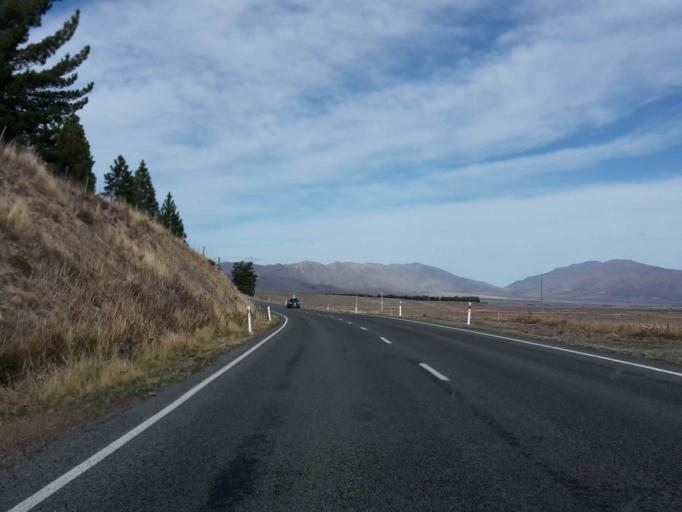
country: NZ
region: Canterbury
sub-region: Timaru District
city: Pleasant Point
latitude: -44.0635
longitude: 170.5041
